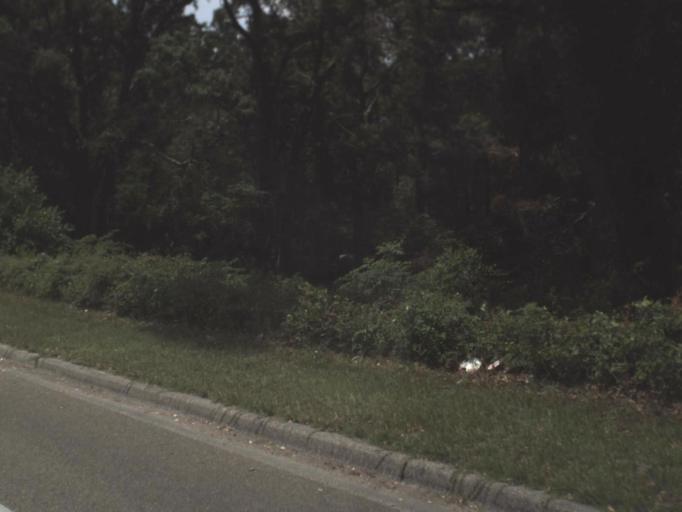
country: US
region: Florida
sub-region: Taylor County
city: Perry
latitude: 30.0821
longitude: -83.5672
